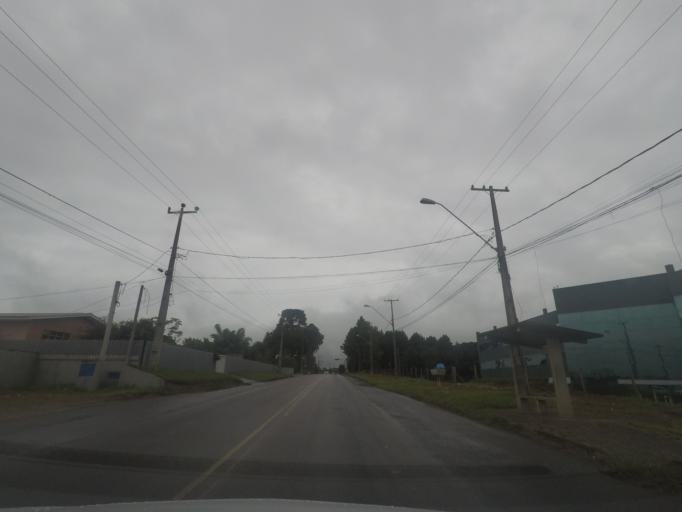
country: BR
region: Parana
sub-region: Campina Grande Do Sul
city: Campina Grande do Sul
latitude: -25.3299
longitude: -49.0783
